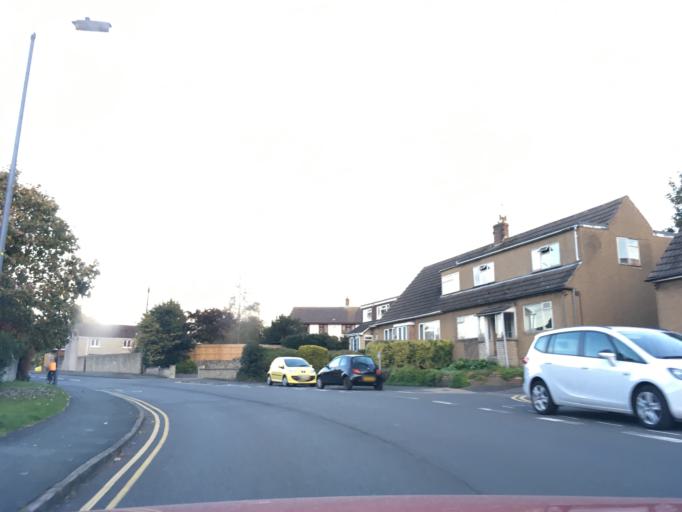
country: GB
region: England
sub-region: South Gloucestershire
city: Stoke Gifford
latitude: 51.5158
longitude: -2.5429
